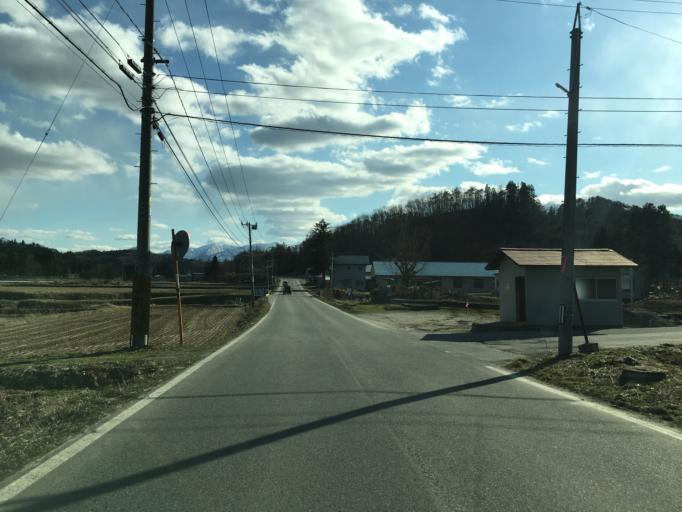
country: JP
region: Yamagata
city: Nagai
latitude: 37.9900
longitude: 140.0045
